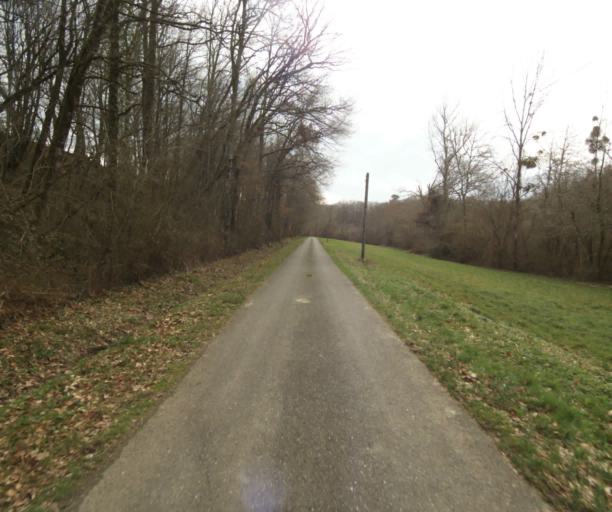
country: FR
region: Midi-Pyrenees
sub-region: Departement du Gers
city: Eauze
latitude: 43.9238
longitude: 0.0630
